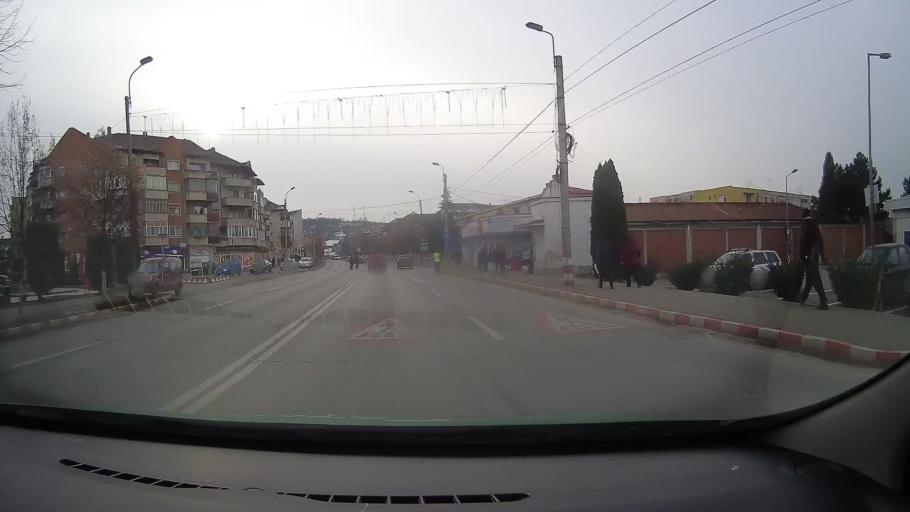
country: RO
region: Hunedoara
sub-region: Municipiul Orastie
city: Orastie
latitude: 45.8398
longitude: 23.1918
